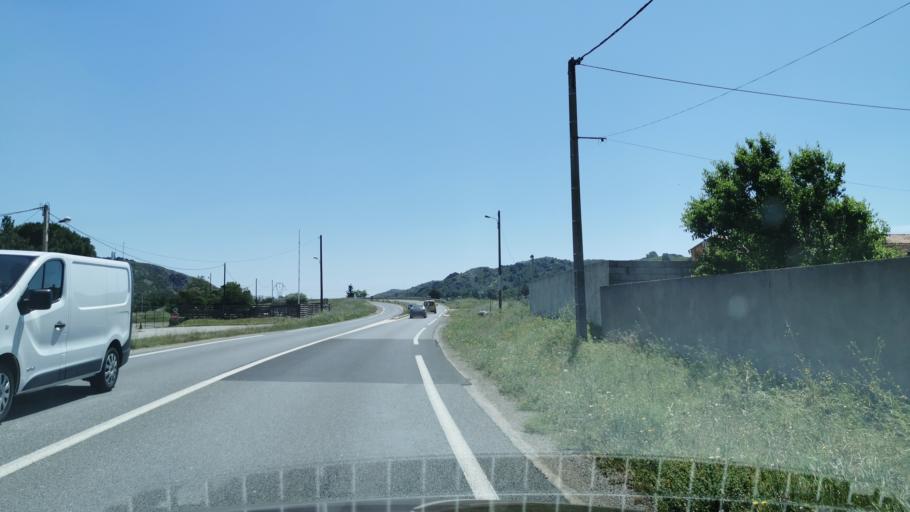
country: FR
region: Languedoc-Roussillon
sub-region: Departement de l'Aude
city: Marcorignan
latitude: 43.1829
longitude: 2.9415
